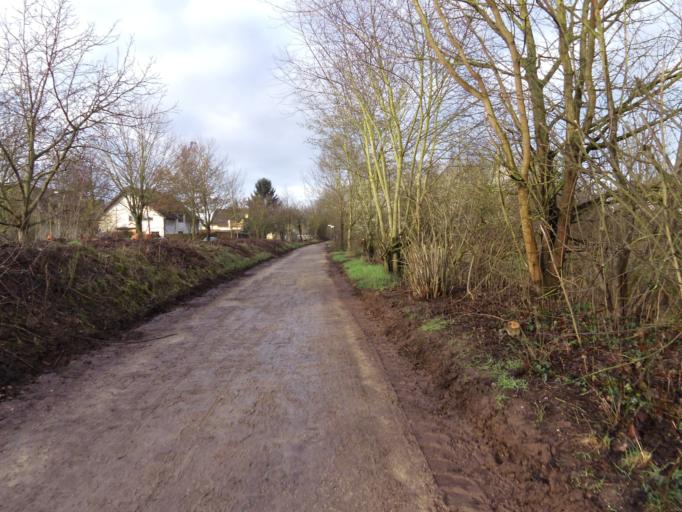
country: DE
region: Rheinland-Pfalz
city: Kleinniedesheim
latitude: 49.6073
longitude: 8.3256
